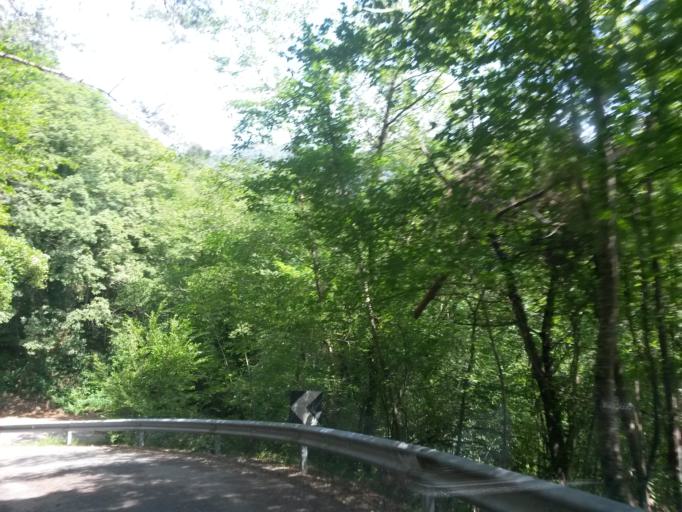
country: IT
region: Lombardy
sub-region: Provincia di Brescia
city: Gardola
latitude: 45.7812
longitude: 10.7139
